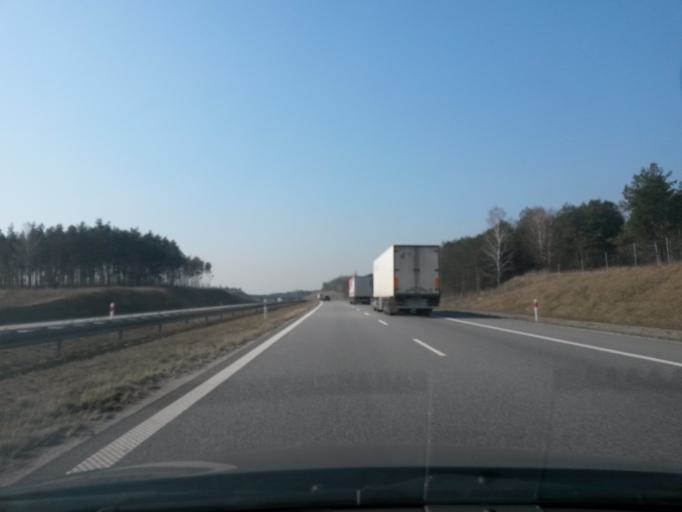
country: PL
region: Lodz Voivodeship
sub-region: powiat Lowicki
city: Lyszkowice
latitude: 51.9646
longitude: 19.8574
